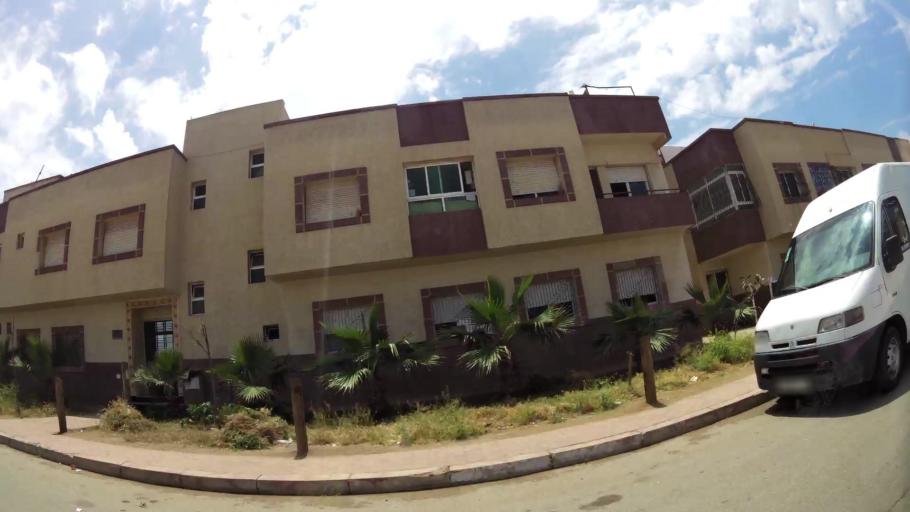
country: MA
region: Rabat-Sale-Zemmour-Zaer
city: Sale
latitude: 34.0475
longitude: -6.8245
